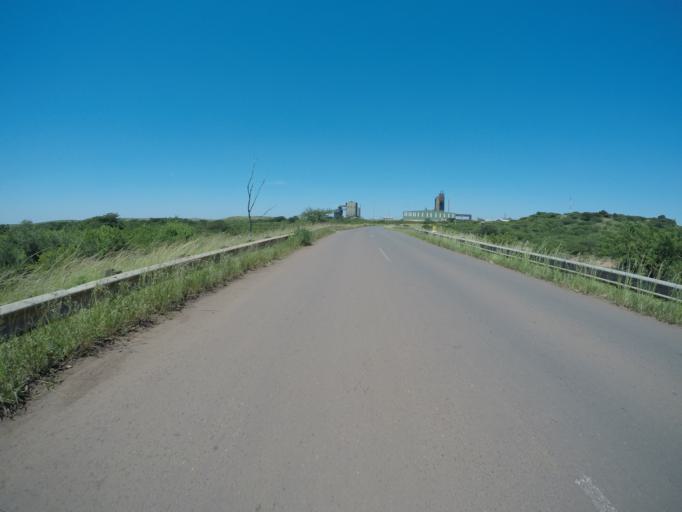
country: ZA
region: KwaZulu-Natal
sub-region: uThungulu District Municipality
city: Empangeni
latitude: -28.7166
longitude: 31.8677
